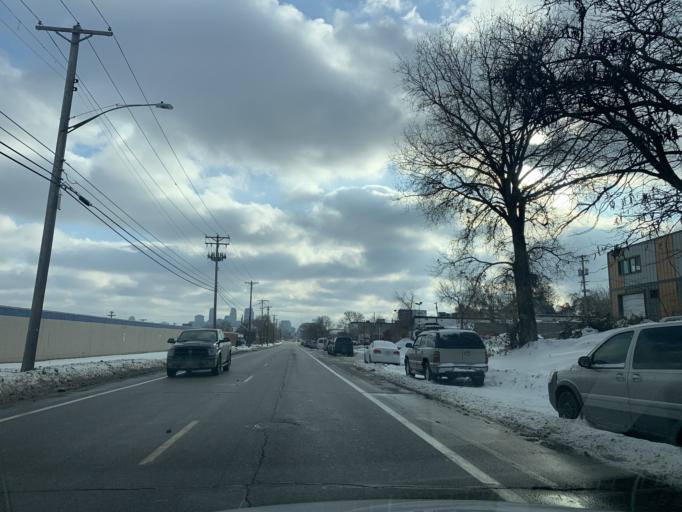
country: US
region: Minnesota
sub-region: Anoka County
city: Columbia Heights
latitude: 45.0163
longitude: -93.2810
